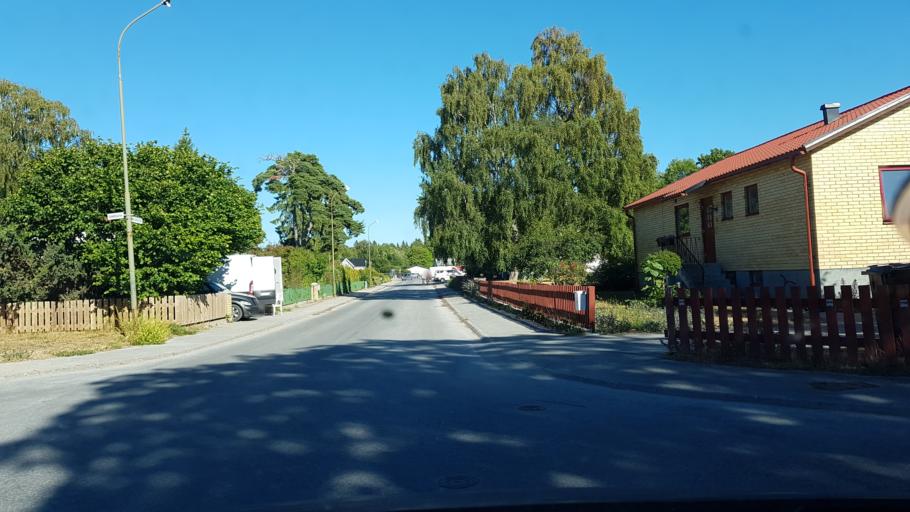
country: SE
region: Gotland
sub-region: Gotland
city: Vibble
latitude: 57.6018
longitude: 18.2482
